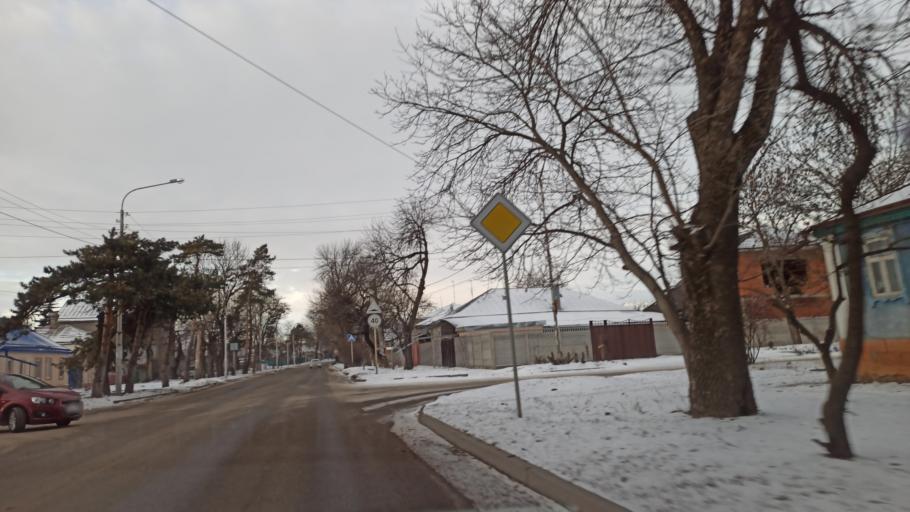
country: RU
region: Stavropol'skiy
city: Yessentukskaya
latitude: 44.0402
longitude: 42.8769
